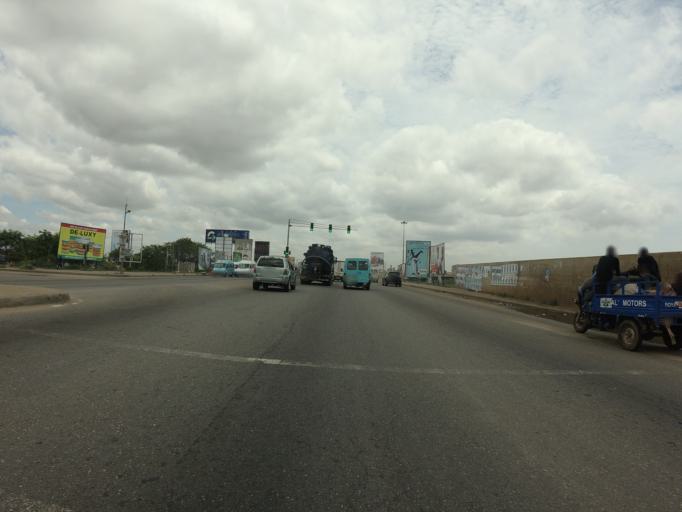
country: GH
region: Greater Accra
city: Gbawe
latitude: 5.5710
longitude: -0.2833
